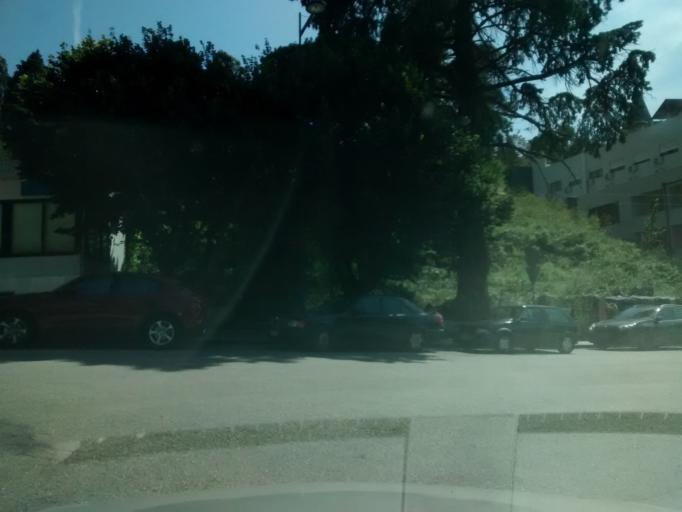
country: PT
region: Aveiro
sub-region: Mealhada
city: Pampilhosa do Botao
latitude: 40.3831
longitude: -8.3758
